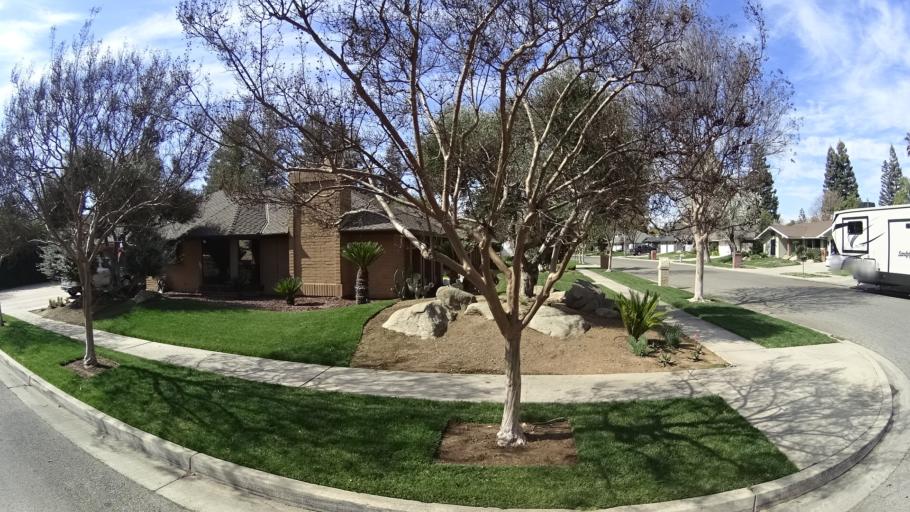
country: US
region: California
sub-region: Fresno County
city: Clovis
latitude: 36.8619
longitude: -119.7697
